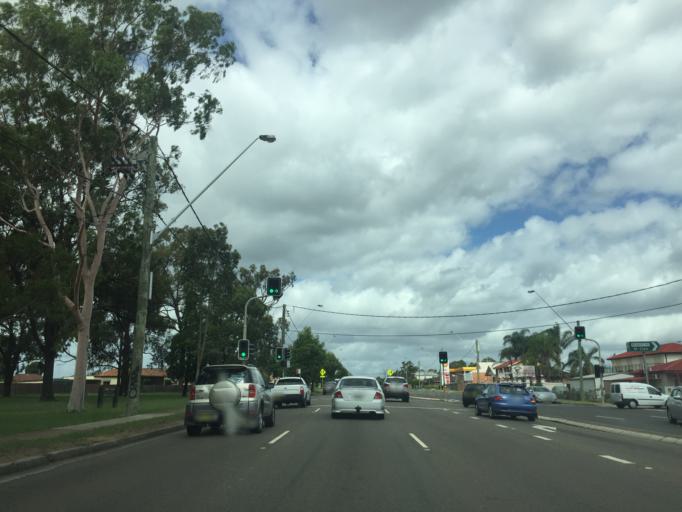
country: AU
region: New South Wales
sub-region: Blacktown
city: Mount Druitt
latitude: -33.7746
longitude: 150.7935
